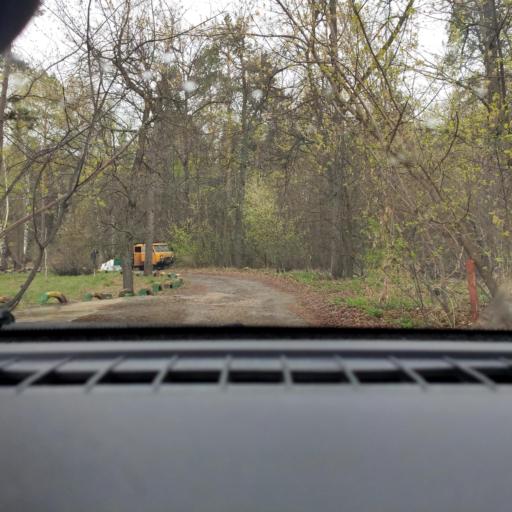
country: RU
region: Samara
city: Zhigulevsk
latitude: 53.4958
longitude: 49.4708
